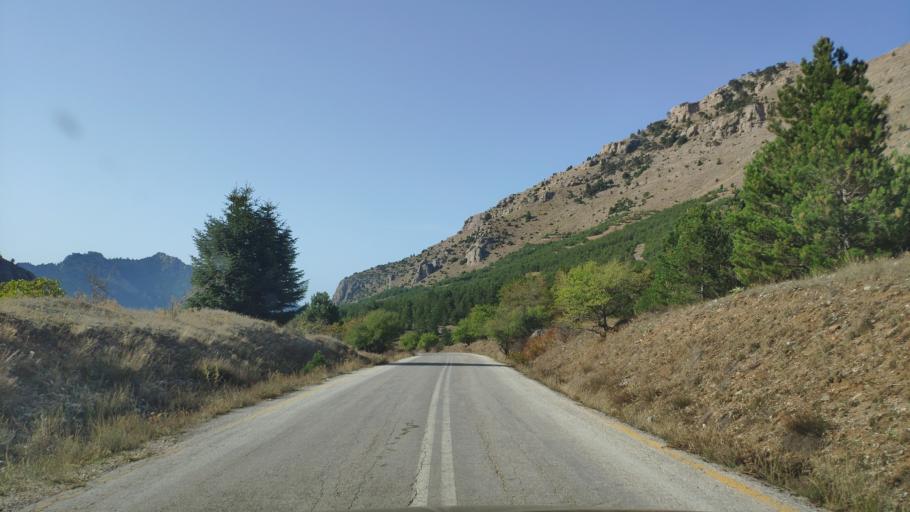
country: GR
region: West Greece
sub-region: Nomos Achaias
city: Aiyira
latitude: 38.0383
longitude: 22.3973
